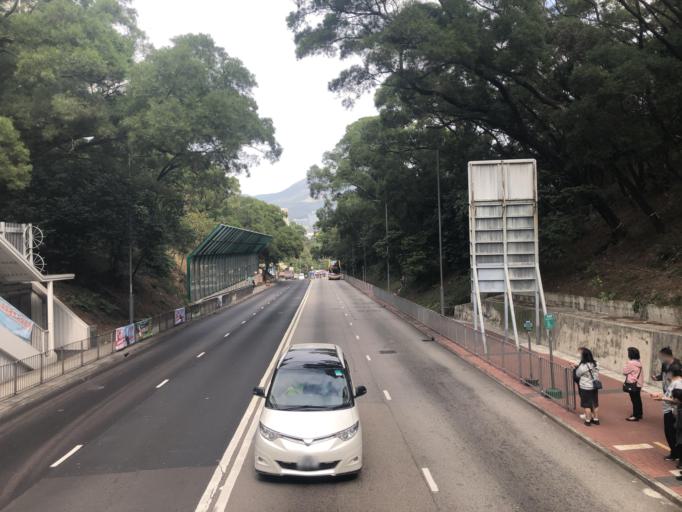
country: HK
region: Tsuen Wan
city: Tsuen Wan
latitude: 22.3533
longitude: 114.0988
